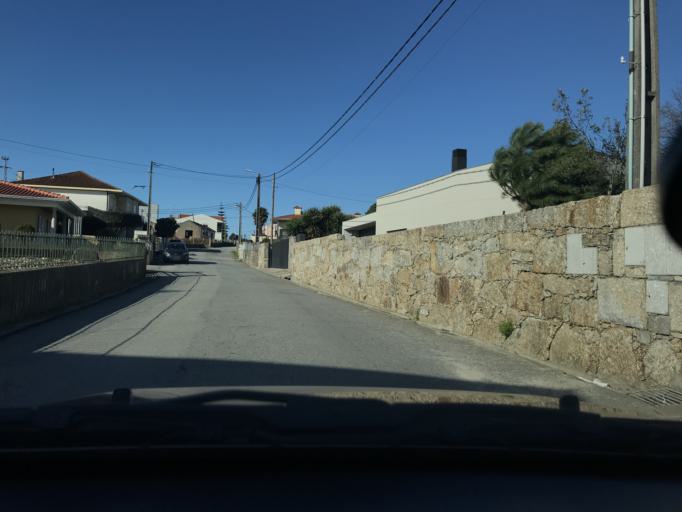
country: PT
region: Braga
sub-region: Vila Nova de Famalicao
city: Vila Nova de Famalicao
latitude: 41.4170
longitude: -8.5099
